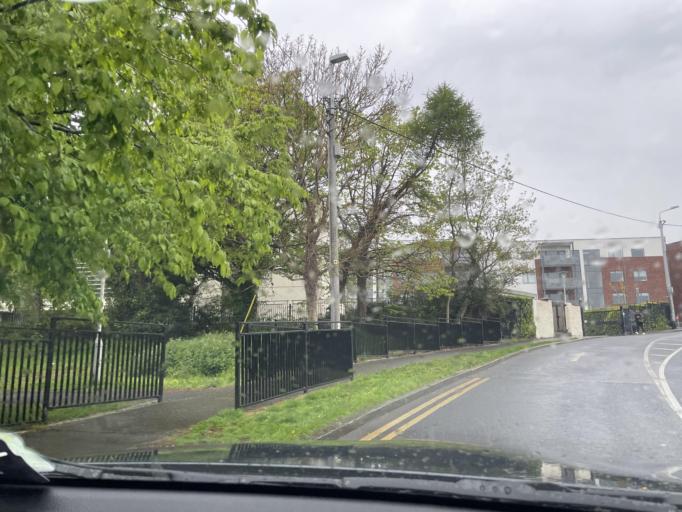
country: IE
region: Leinster
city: Dundrum
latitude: 53.2925
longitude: -6.2477
